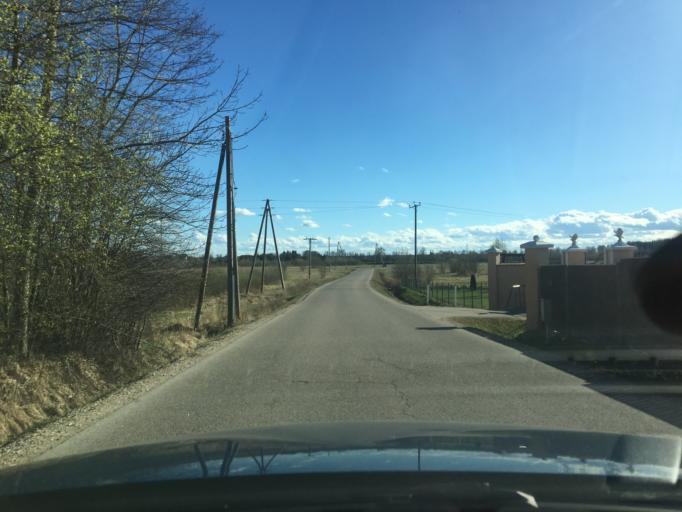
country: LV
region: Salaspils
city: Salaspils
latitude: 56.8700
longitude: 24.3235
